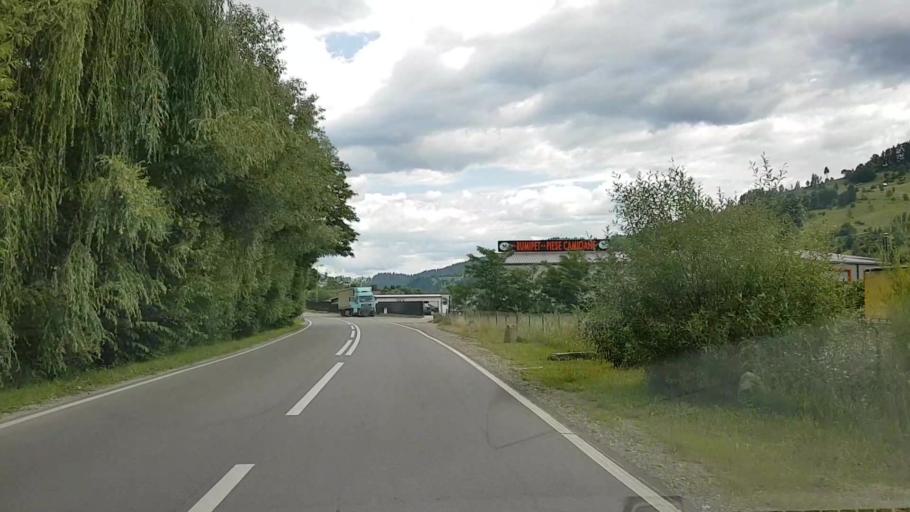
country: RO
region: Neamt
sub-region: Comuna Borca
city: Borca
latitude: 47.1709
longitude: 25.7964
